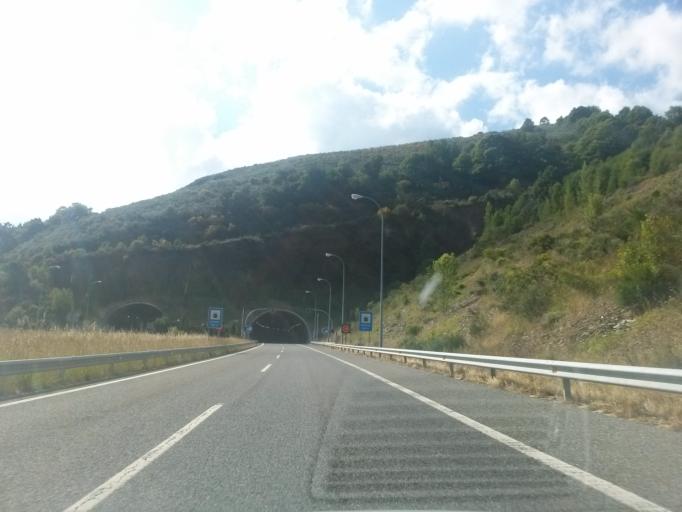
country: ES
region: Galicia
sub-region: Provincia de Lugo
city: Becerrea
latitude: 42.7835
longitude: -7.1039
